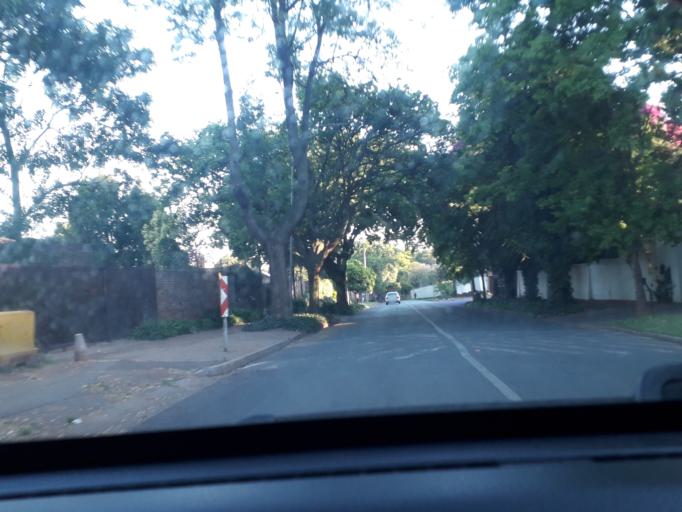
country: ZA
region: Gauteng
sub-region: City of Johannesburg Metropolitan Municipality
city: Johannesburg
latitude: -26.1621
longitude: 28.0501
